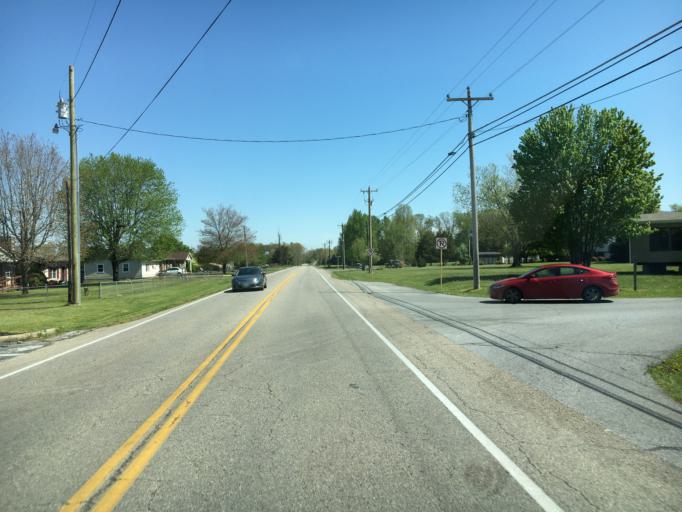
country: US
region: Virginia
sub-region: Augusta County
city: Crimora
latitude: 38.1761
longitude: -78.8465
